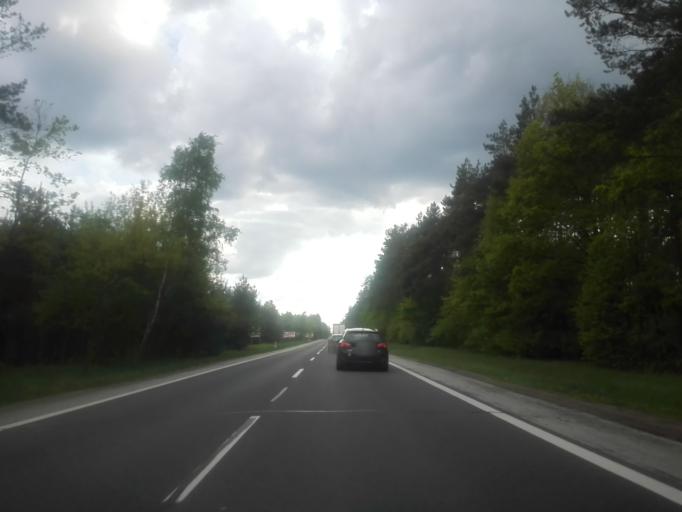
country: PL
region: Masovian Voivodeship
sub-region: Powiat ostrowski
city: Ostrow Mazowiecka
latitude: 52.7700
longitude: 21.8255
